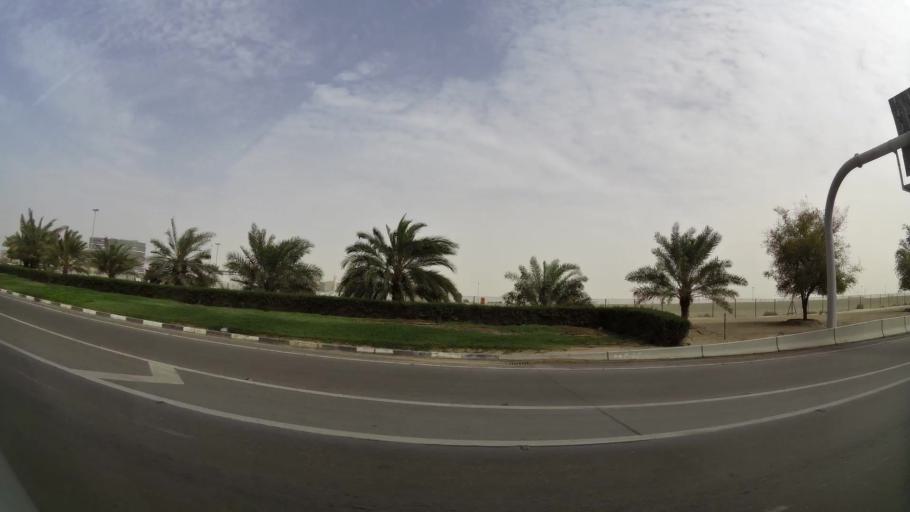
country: AE
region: Abu Dhabi
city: Abu Dhabi
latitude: 24.3687
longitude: 54.5253
